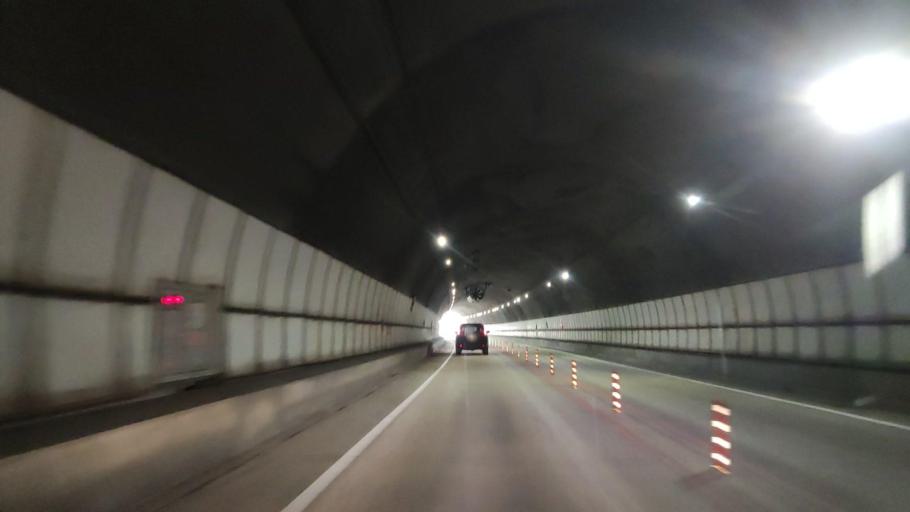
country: JP
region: Yamagata
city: Shinjo
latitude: 38.6799
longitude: 140.3184
